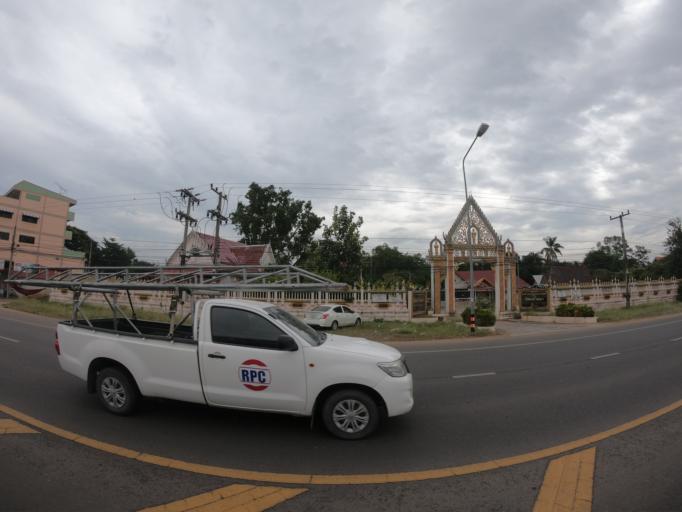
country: TH
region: Roi Et
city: Roi Et
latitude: 16.0767
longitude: 103.6887
